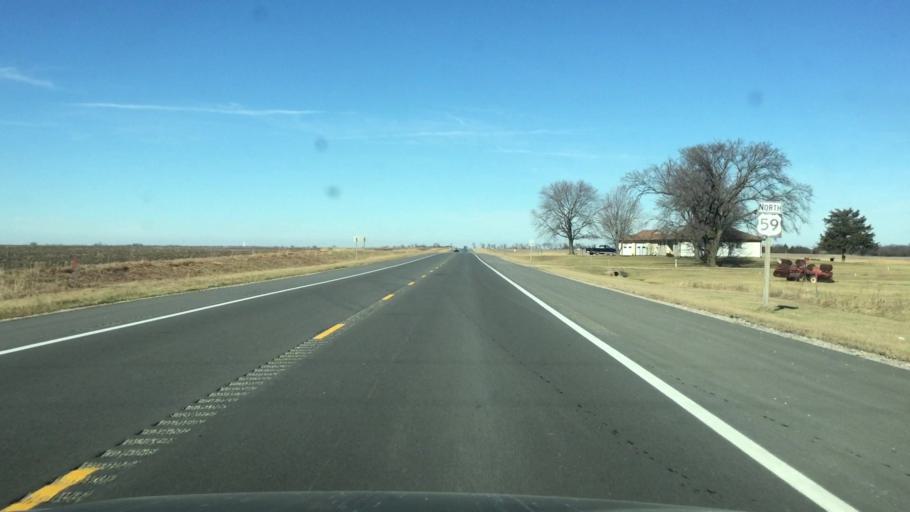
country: US
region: Kansas
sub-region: Anderson County
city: Garnett
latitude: 38.4341
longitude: -95.2487
